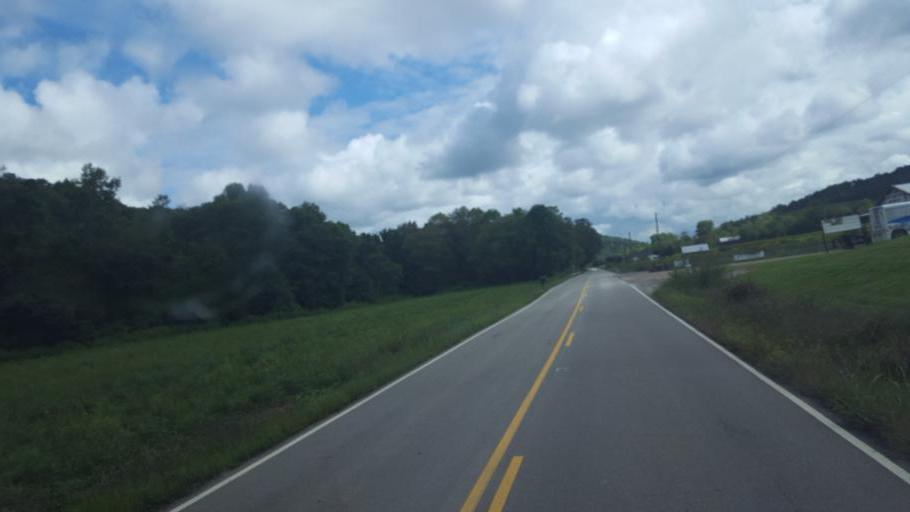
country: US
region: Ohio
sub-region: Scioto County
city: Sciotodale
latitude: 38.8886
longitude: -82.7589
